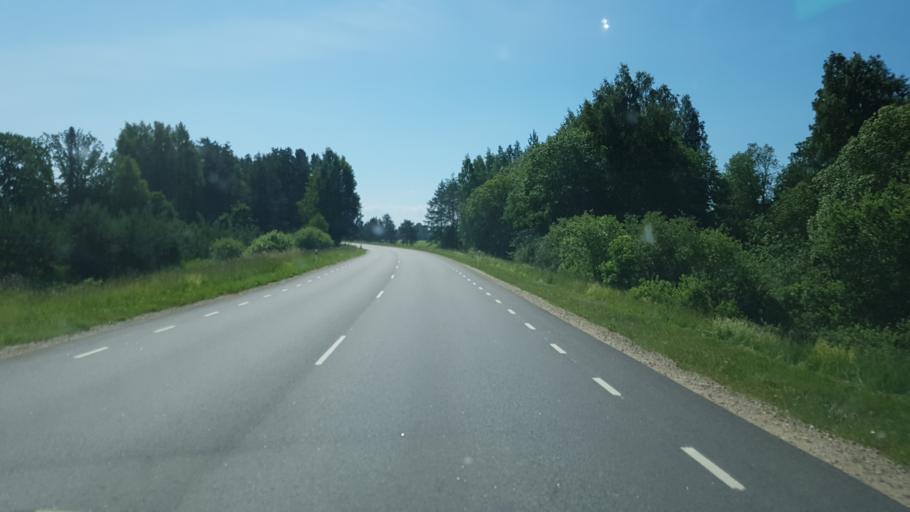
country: EE
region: Tartu
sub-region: UElenurme vald
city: Ulenurme
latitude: 58.3174
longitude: 26.9863
